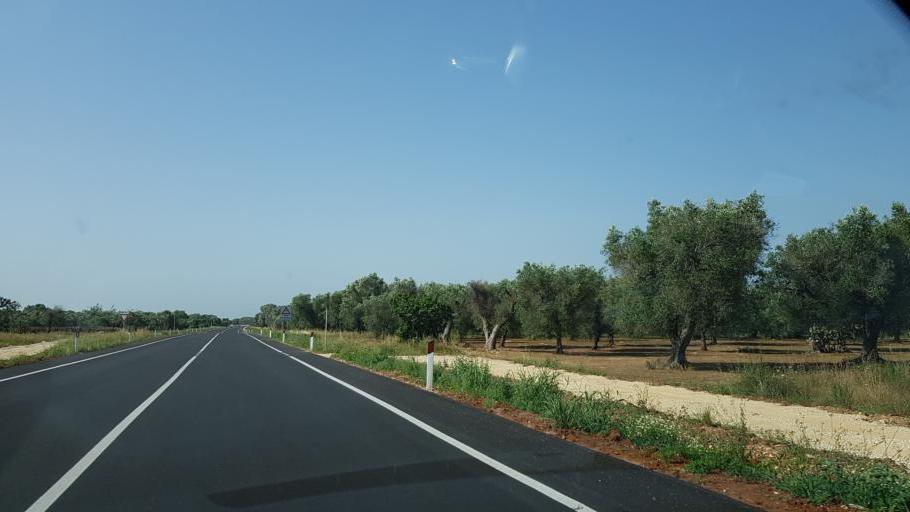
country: IT
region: Apulia
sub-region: Provincia di Brindisi
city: San Pancrazio Salentino
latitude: 40.4712
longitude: 17.8379
